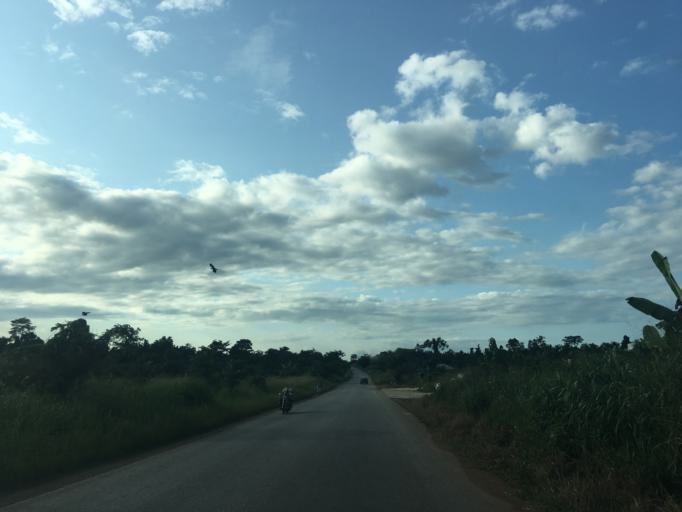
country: GH
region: Western
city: Bibiani
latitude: 6.3089
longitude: -2.2506
